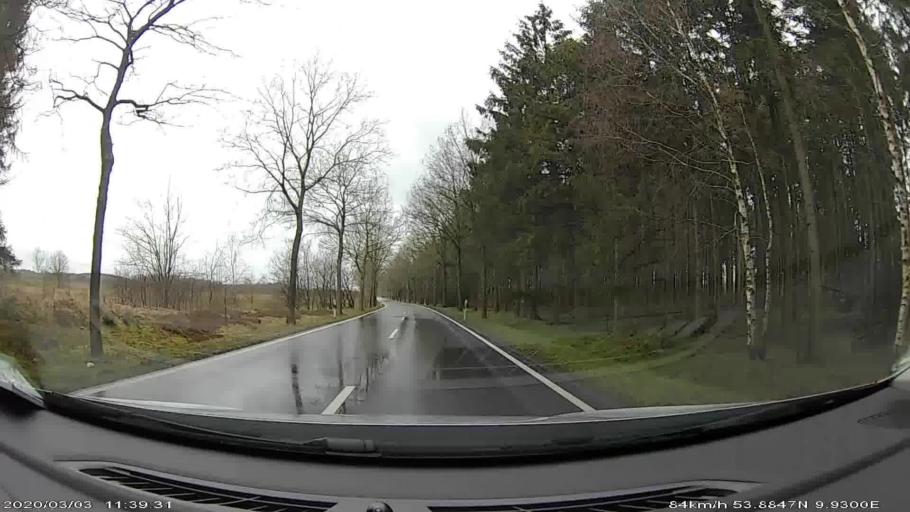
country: DE
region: Schleswig-Holstein
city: Nutzen
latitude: 53.8852
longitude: 9.9252
